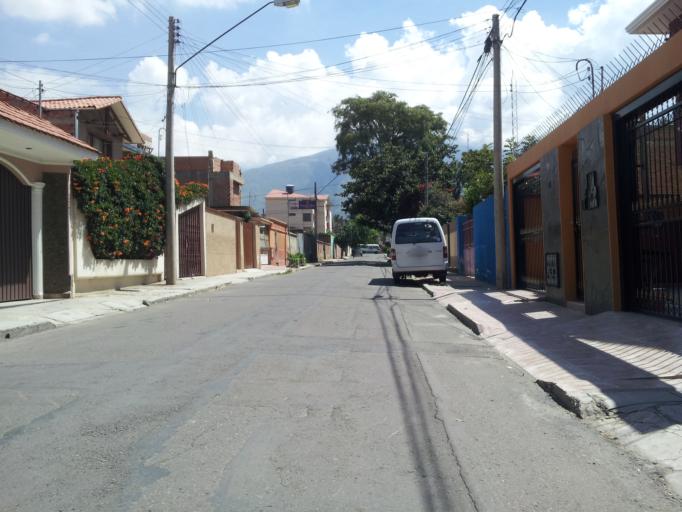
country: BO
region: Cochabamba
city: Cochabamba
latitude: -17.3734
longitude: -66.1716
